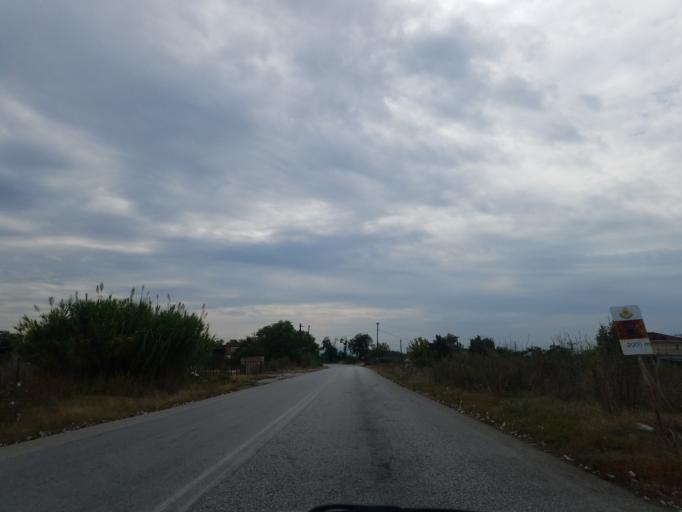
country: GR
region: Thessaly
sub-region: Nomos Kardhitsas
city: Sofades
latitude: 39.3308
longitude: 22.0876
